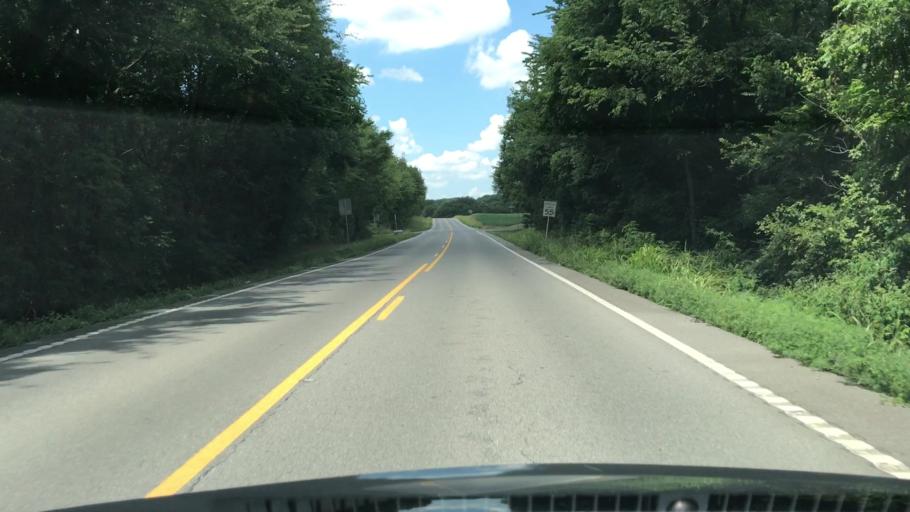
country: US
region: Tennessee
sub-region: Williamson County
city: Nolensville
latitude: 35.8525
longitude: -86.6344
